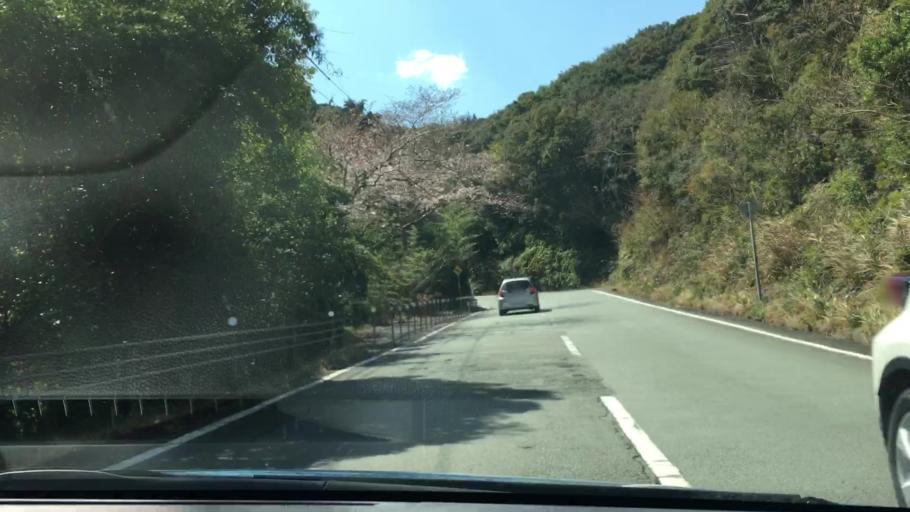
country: JP
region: Mie
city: Toba
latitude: 34.4487
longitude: 136.8797
